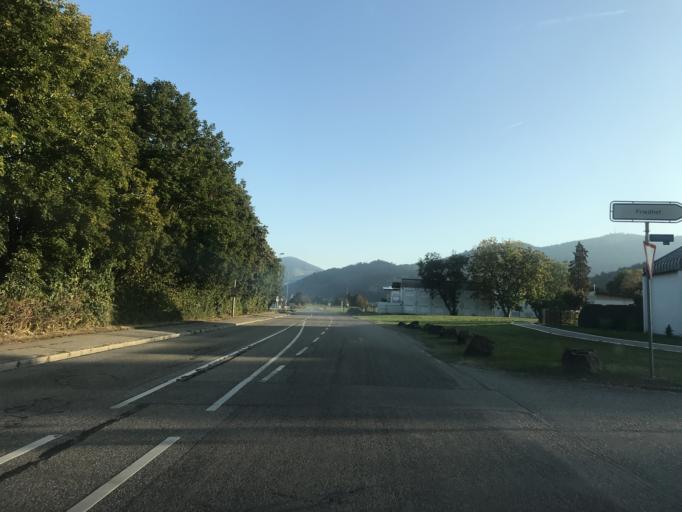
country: DE
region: Baden-Wuerttemberg
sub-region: Freiburg Region
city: Hausen
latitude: 47.6632
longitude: 7.8383
